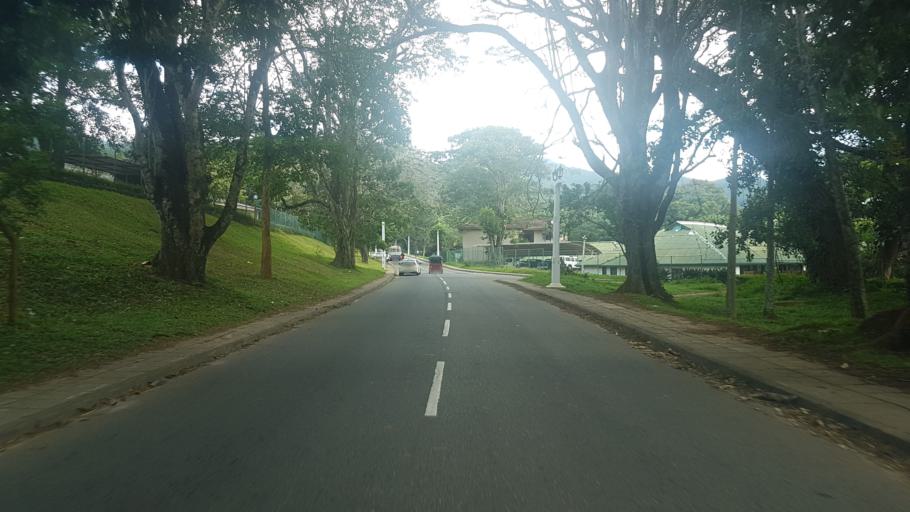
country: LK
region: Central
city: Kandy
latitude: 7.2641
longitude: 80.5971
